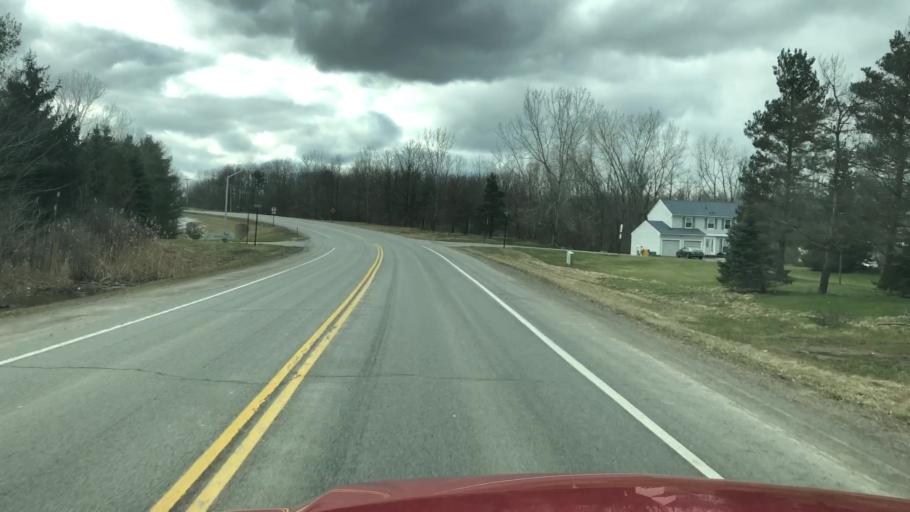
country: US
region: New York
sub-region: Wayne County
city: Macedon
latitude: 43.1275
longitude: -77.3494
